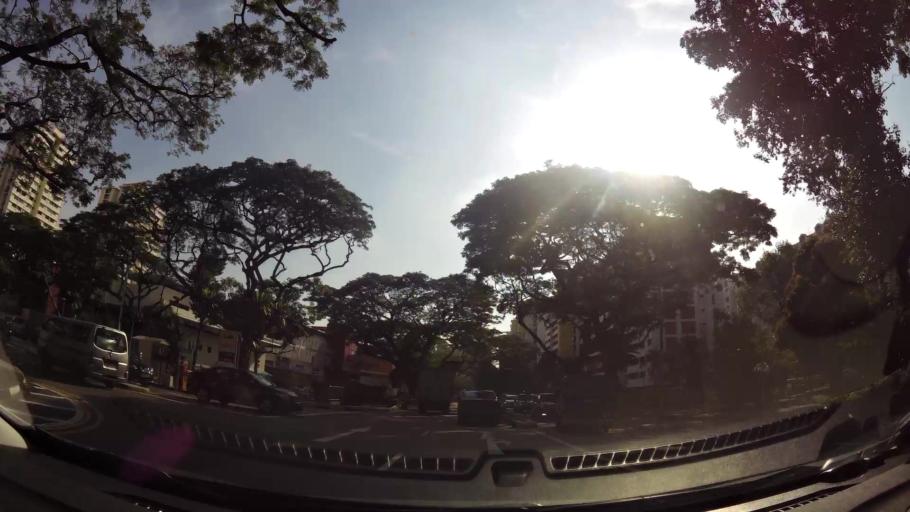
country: SG
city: Singapore
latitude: 1.3398
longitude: 103.8549
